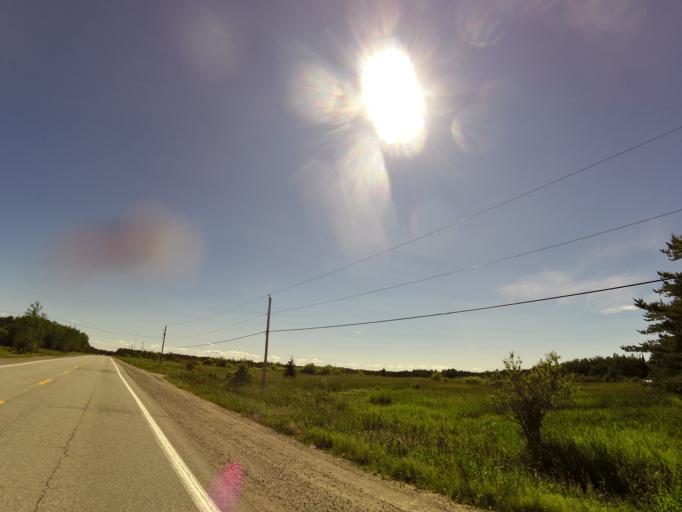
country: CA
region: Quebec
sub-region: Abitibi-Temiscamingue
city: Senneterre
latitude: 48.2604
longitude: -77.3297
